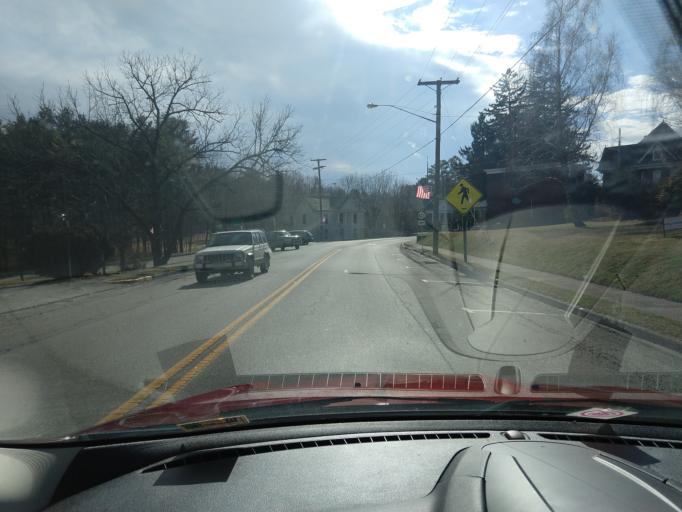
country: US
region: Virginia
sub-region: Floyd County
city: Floyd
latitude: 36.9127
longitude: -80.3140
